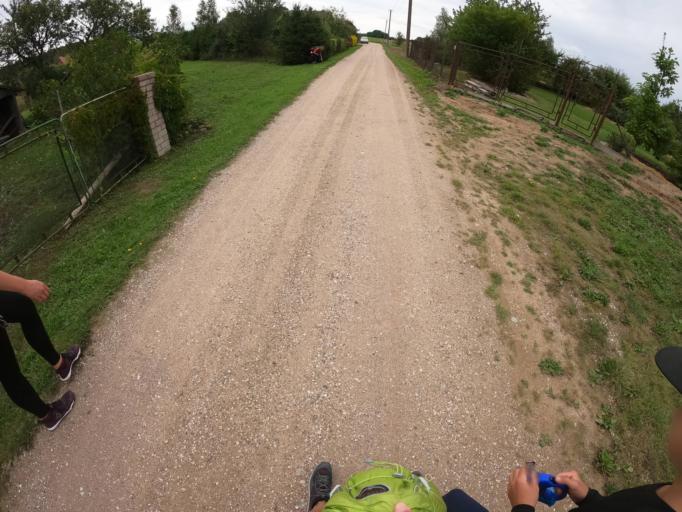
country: LV
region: Kuldigas Rajons
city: Kuldiga
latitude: 56.9478
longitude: 21.9792
